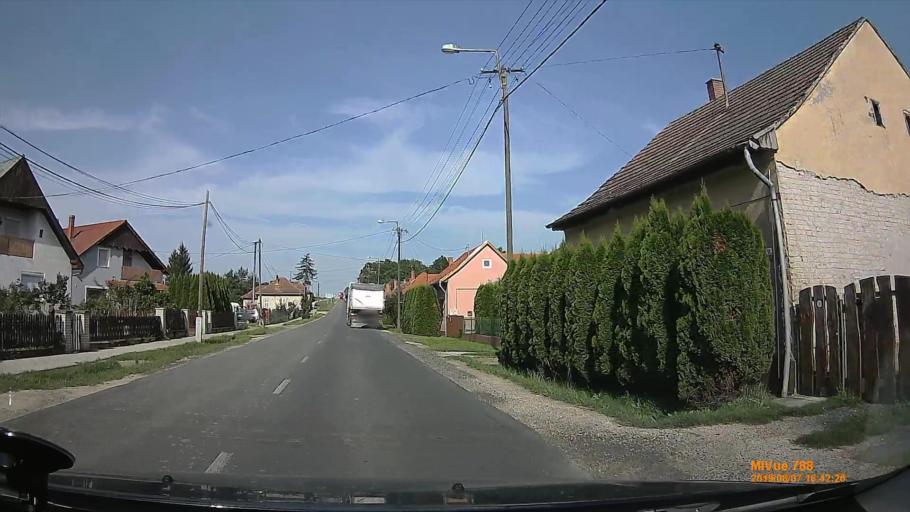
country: HU
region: Zala
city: Lenti
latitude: 46.6294
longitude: 16.5640
